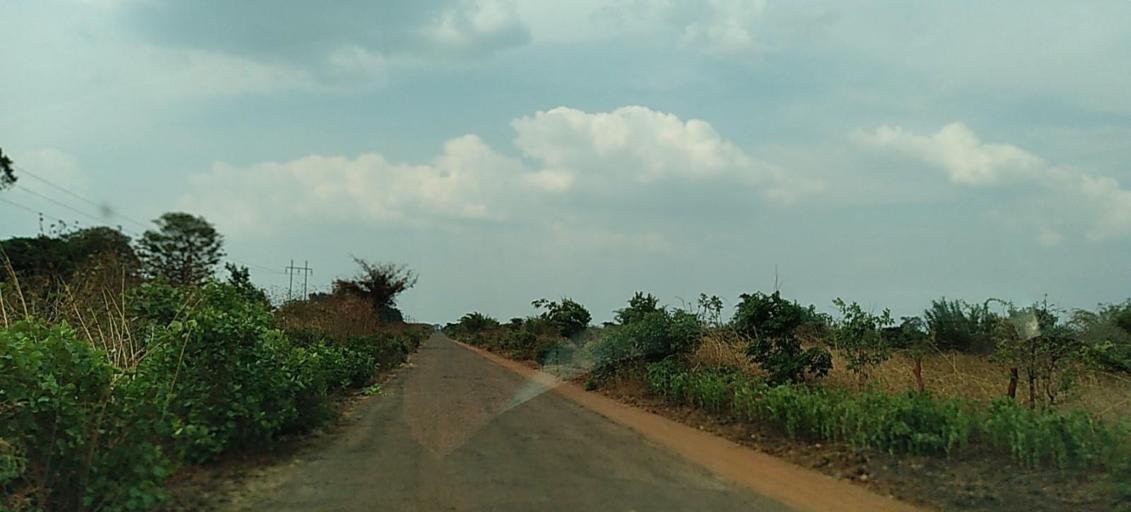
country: ZM
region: Copperbelt
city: Chililabombwe
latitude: -12.3873
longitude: 27.8086
